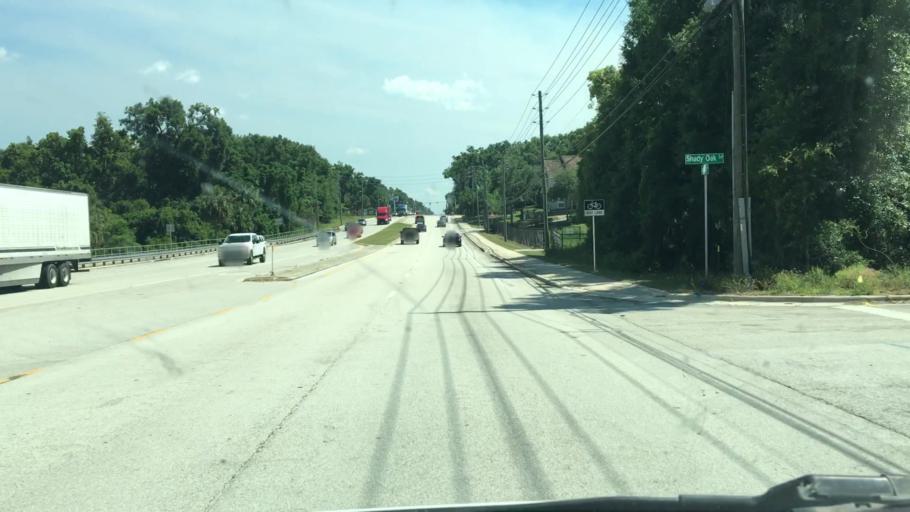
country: US
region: Florida
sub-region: Volusia County
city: North DeLand
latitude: 29.0466
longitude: -81.3249
